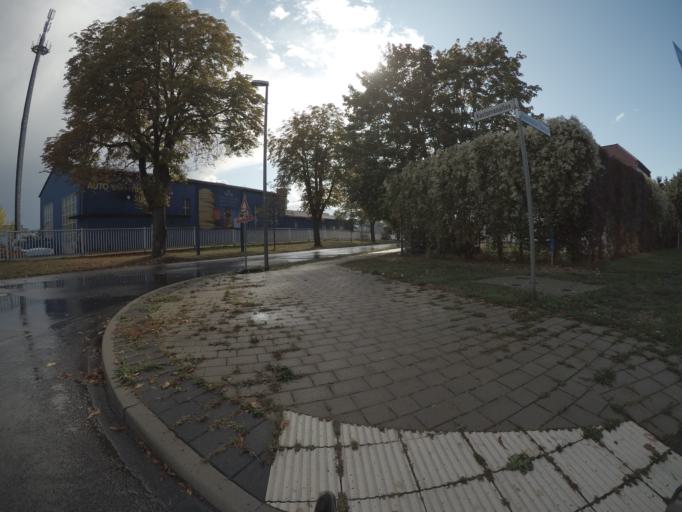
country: DE
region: Brandenburg
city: Strausberg
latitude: 52.5883
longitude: 13.9035
